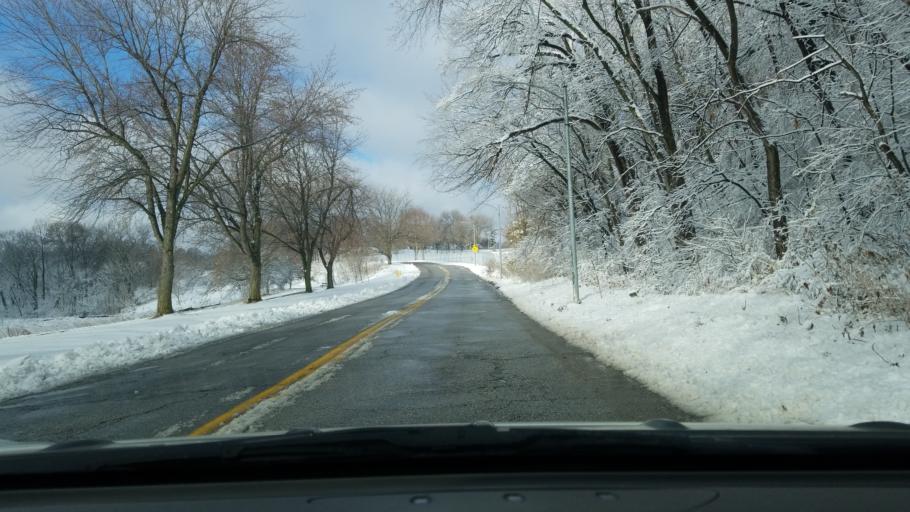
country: US
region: Nebraska
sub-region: Douglas County
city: Omaha
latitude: 41.2182
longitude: -95.9354
